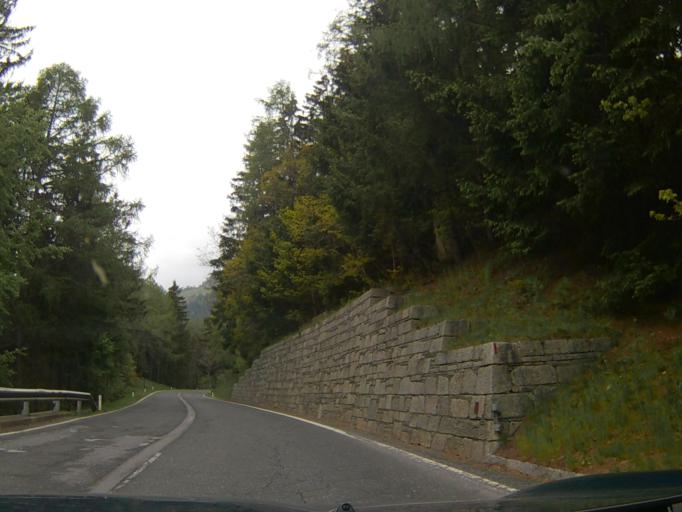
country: AT
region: Carinthia
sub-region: Politischer Bezirk Spittal an der Drau
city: Obervellach
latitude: 46.9416
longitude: 13.1909
